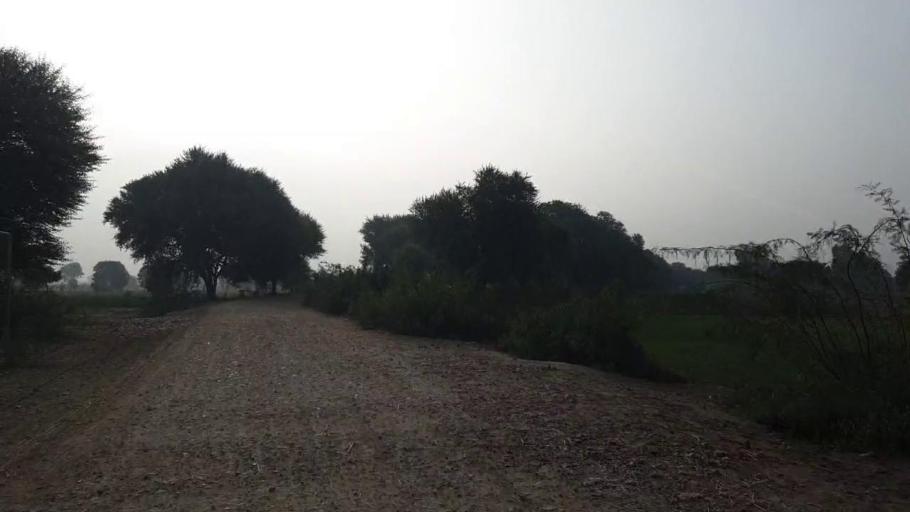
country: PK
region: Sindh
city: Tando Muhammad Khan
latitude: 25.1781
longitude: 68.6024
